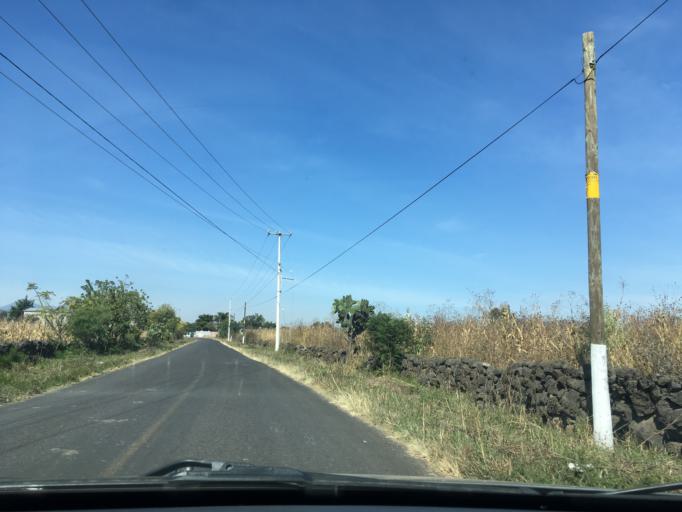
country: MX
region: Michoacan
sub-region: Morelia
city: La Mintzita (Piedra Dura)
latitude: 19.6499
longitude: -101.3046
